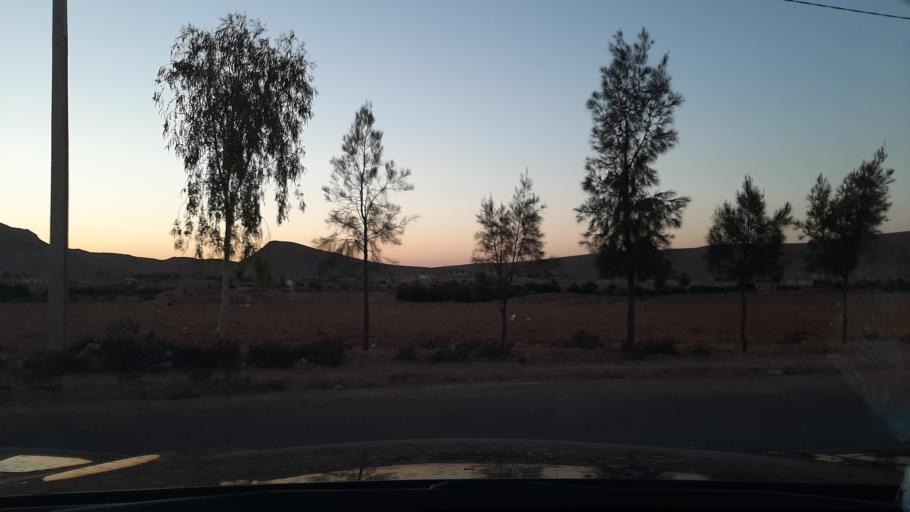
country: TN
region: Qabis
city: Matmata
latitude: 33.5698
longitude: 10.1775
